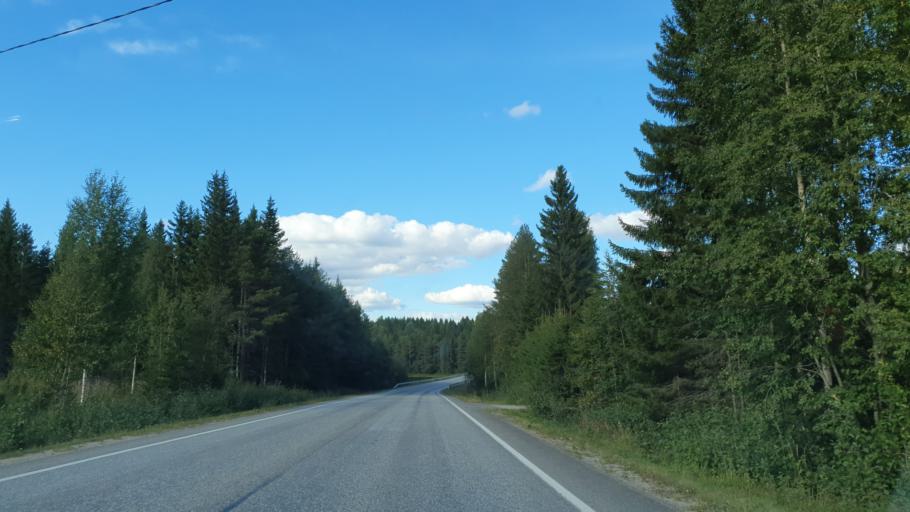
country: FI
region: Kainuu
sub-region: Kehys-Kainuu
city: Kuhmo
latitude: 64.1573
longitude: 29.4641
